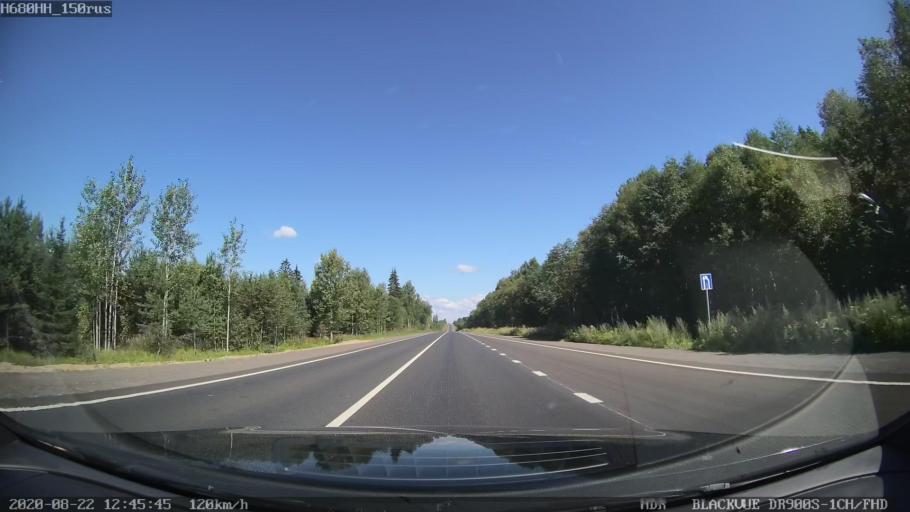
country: RU
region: Tverskaya
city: Rameshki
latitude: 57.4093
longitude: 36.1283
